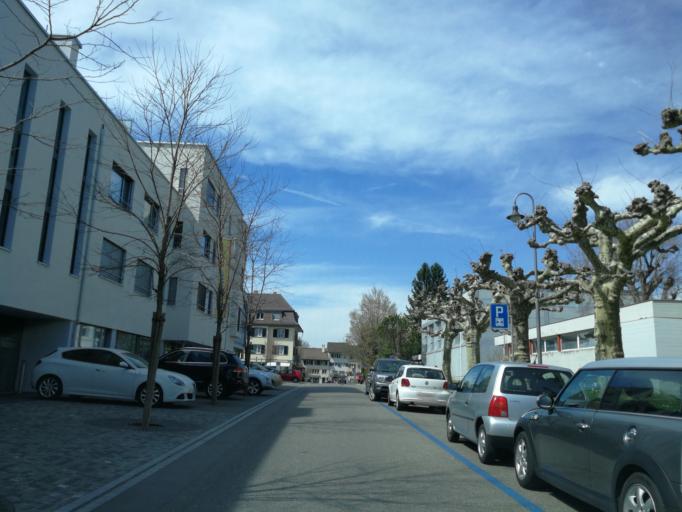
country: CH
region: Zurich
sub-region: Bezirk Meilen
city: Meilen
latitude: 47.2683
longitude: 8.6425
